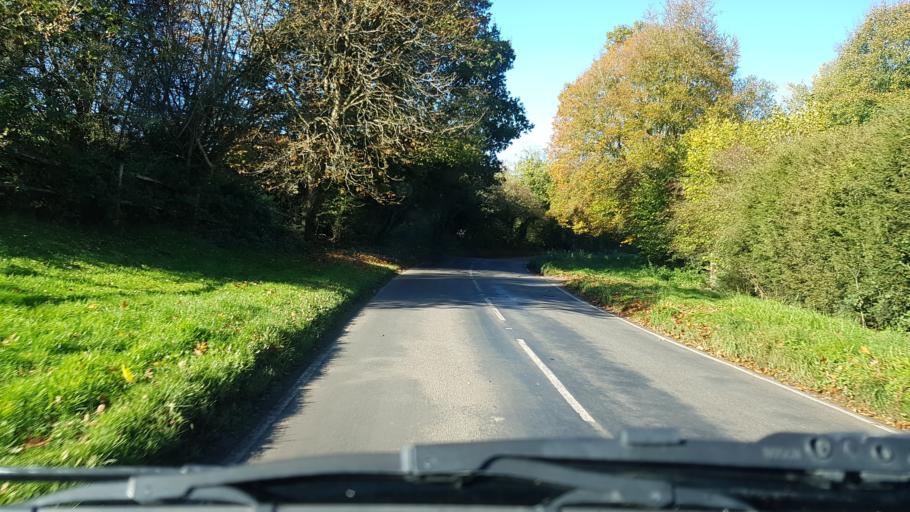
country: GB
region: England
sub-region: Surrey
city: East Horsley
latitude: 51.2062
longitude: -0.4304
